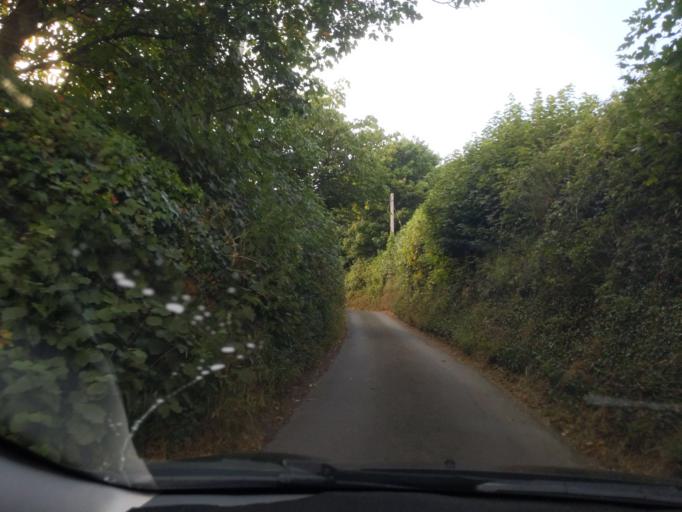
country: GB
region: England
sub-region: Devon
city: Salcombe
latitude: 50.2310
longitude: -3.7977
